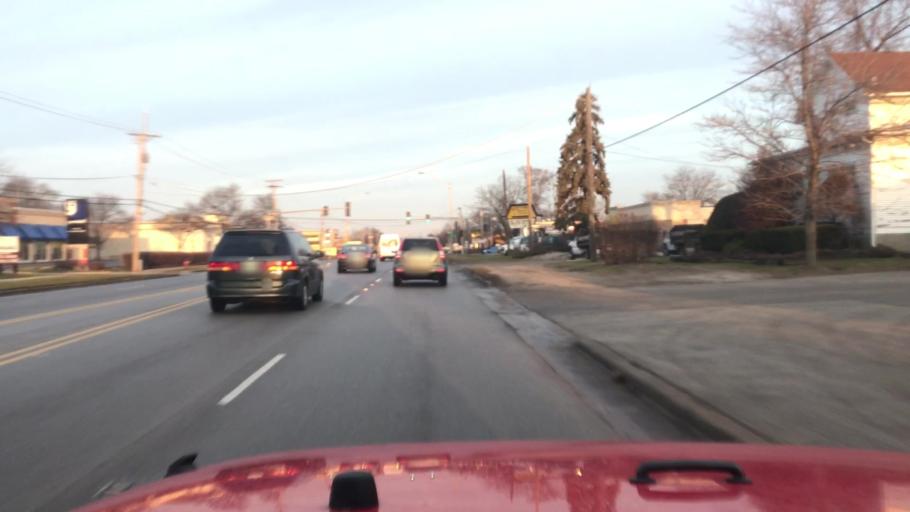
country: US
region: Illinois
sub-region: Cook County
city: Arlington Heights
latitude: 42.1043
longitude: -87.9679
